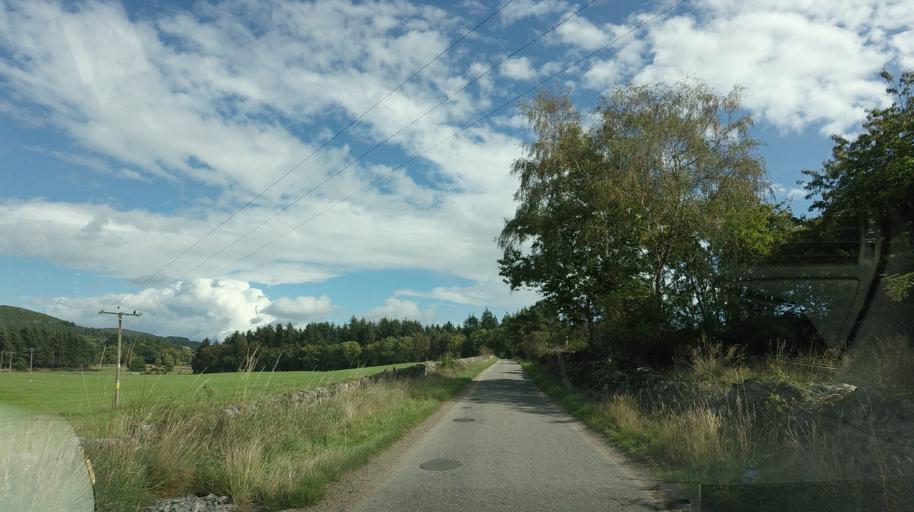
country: GB
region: Scotland
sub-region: Aberdeenshire
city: Banchory
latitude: 57.0773
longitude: -2.5045
